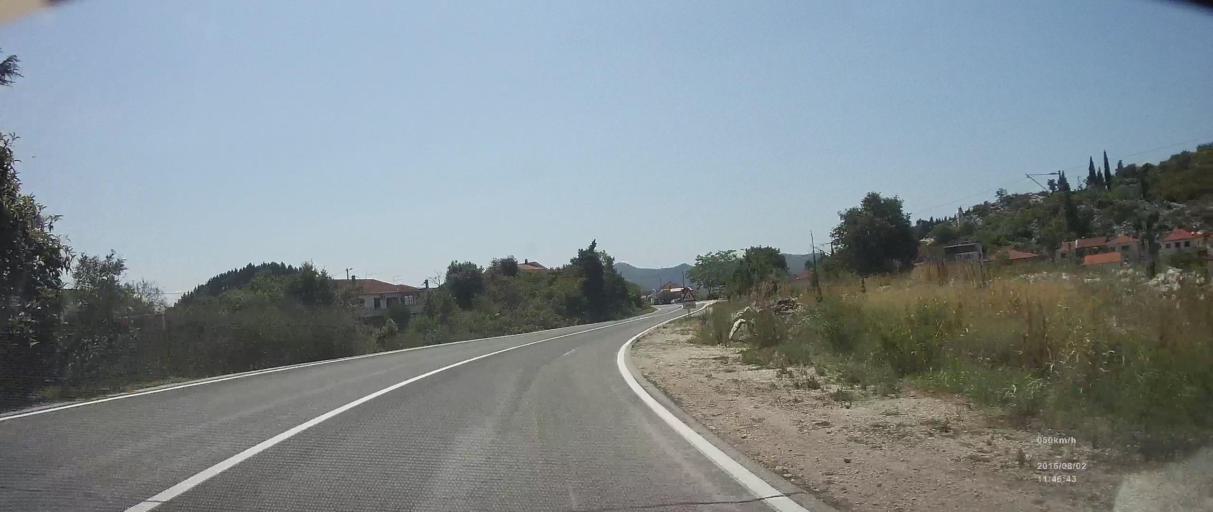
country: HR
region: Dubrovacko-Neretvanska
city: Komin
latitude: 43.0505
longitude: 17.4781
